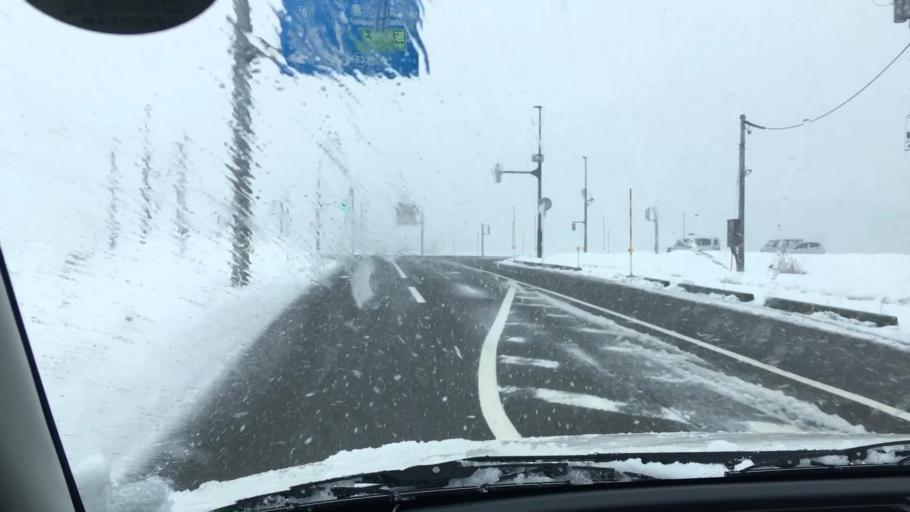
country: JP
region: Niigata
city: Joetsu
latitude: 37.0816
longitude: 138.2344
